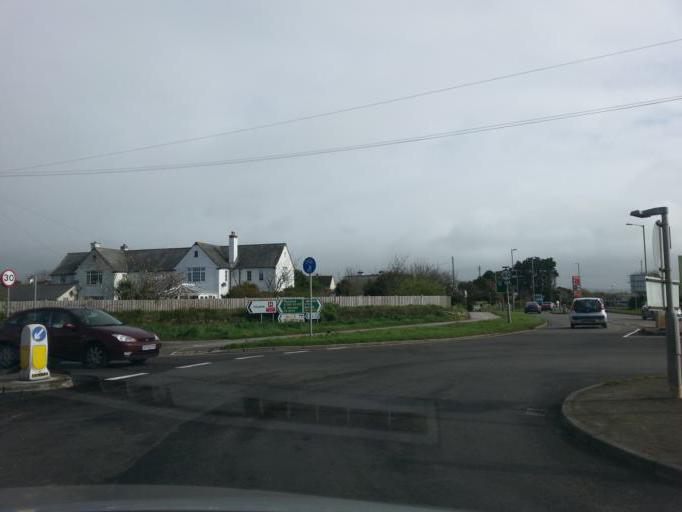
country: GB
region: England
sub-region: Cornwall
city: Helston
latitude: 50.0919
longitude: -5.2643
